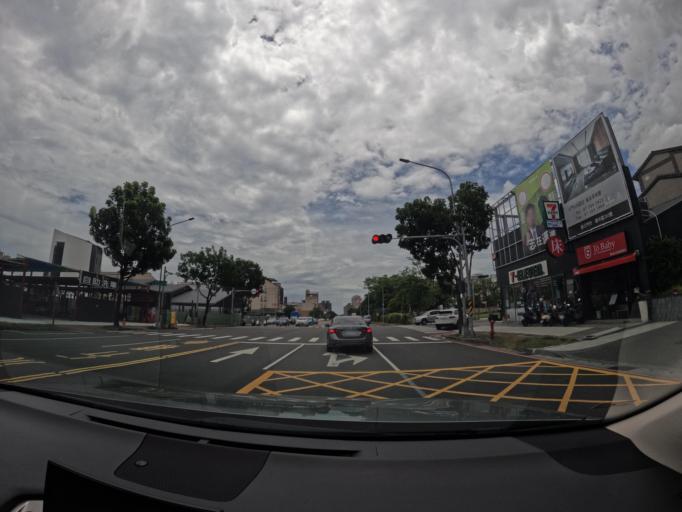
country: TW
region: Kaohsiung
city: Kaohsiung
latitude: 22.7268
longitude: 120.2947
